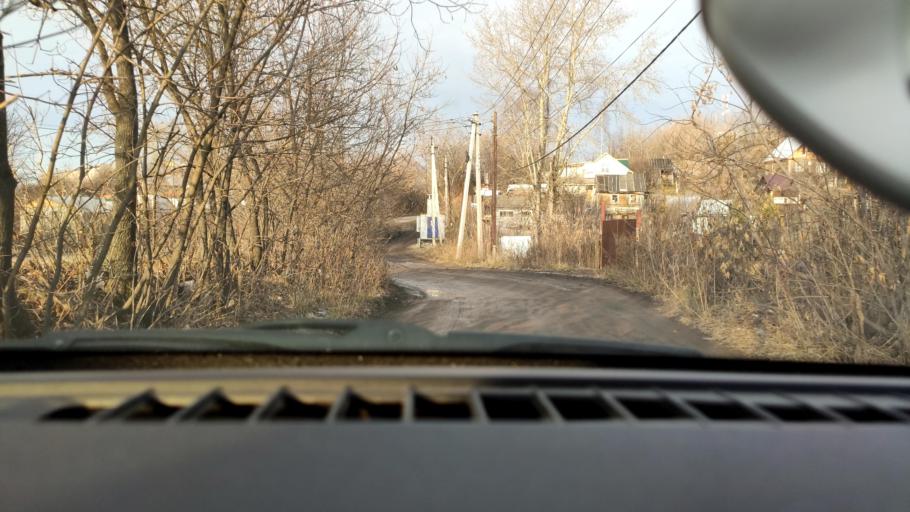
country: RU
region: Perm
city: Kondratovo
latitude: 57.9568
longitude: 56.1526
